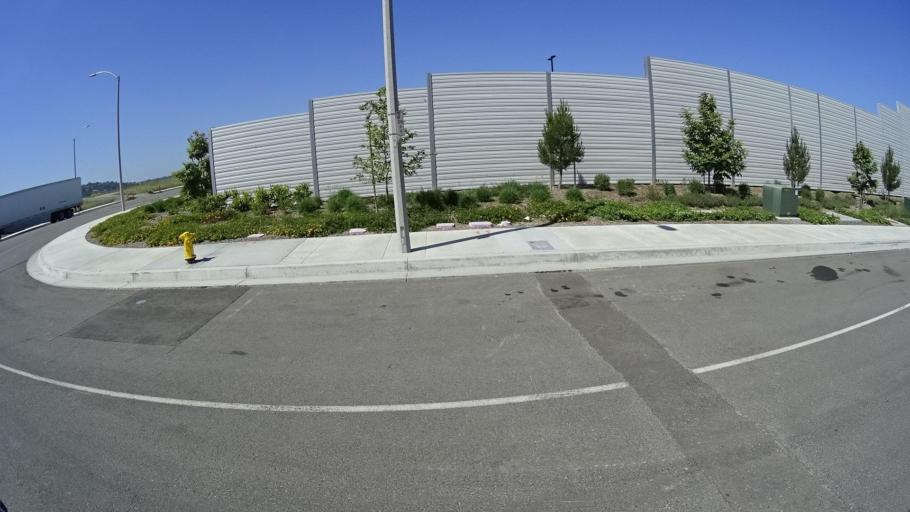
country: US
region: California
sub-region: Los Angeles County
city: Diamond Bar
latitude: 34.0186
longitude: -117.8218
